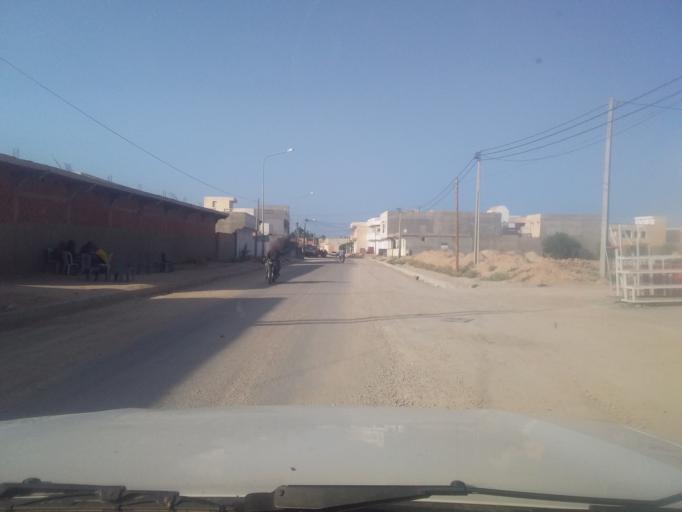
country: TN
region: Qabis
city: Matmata
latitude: 33.6124
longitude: 10.2844
